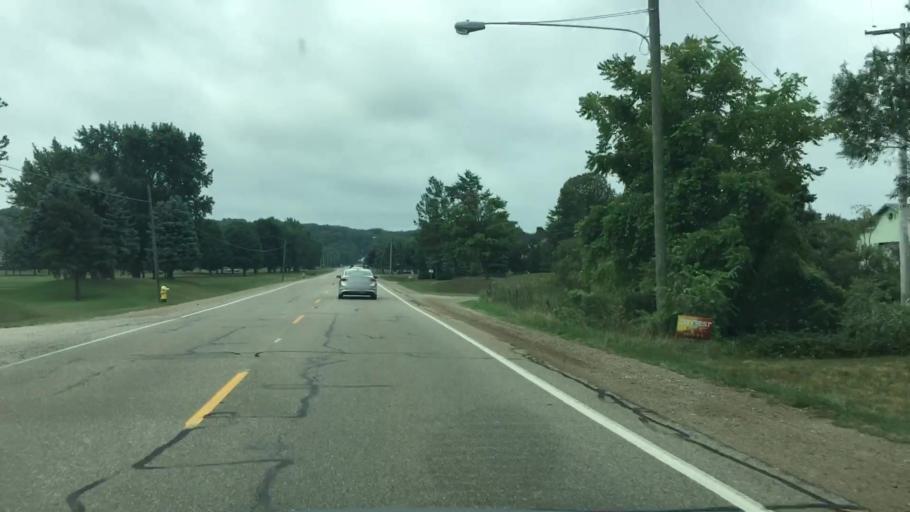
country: US
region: Michigan
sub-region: Ottawa County
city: Jenison
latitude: 42.8804
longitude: -85.8168
